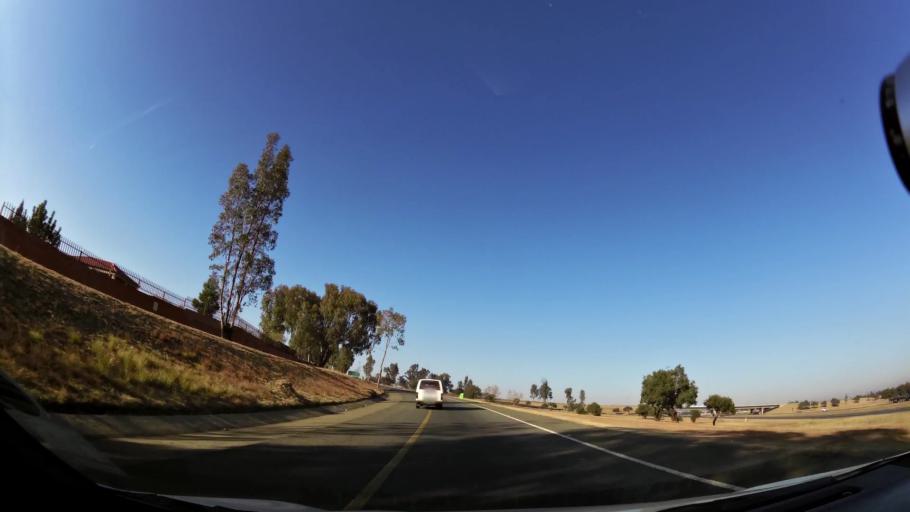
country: ZA
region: Gauteng
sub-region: Ekurhuleni Metropolitan Municipality
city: Germiston
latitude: -26.3487
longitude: 28.1022
